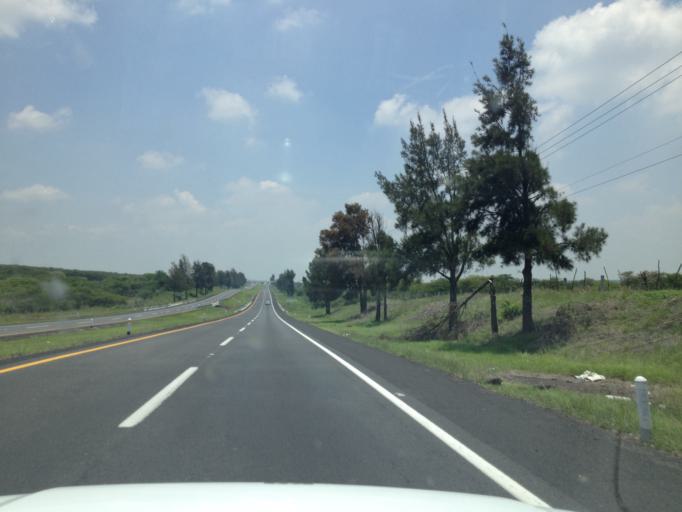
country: MX
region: Michoacan
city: Churintzio
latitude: 20.1602
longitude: -102.1168
